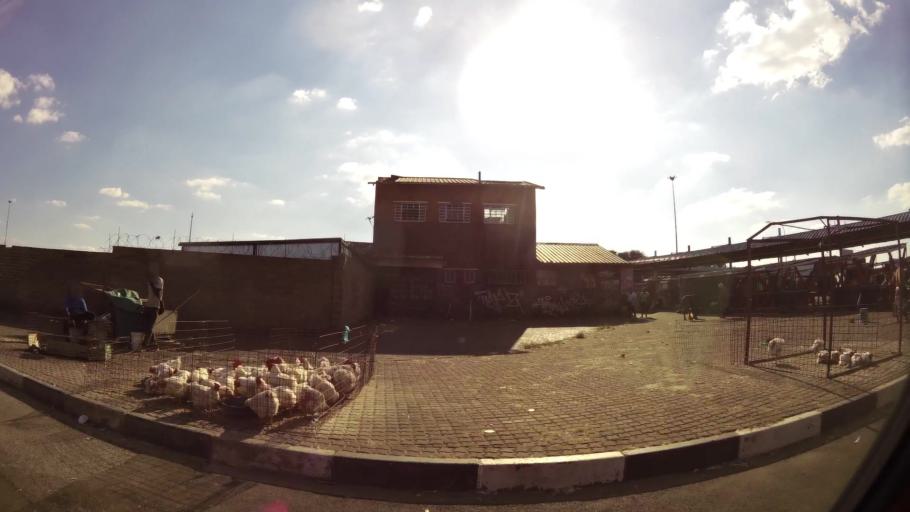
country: ZA
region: Gauteng
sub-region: City of Johannesburg Metropolitan Municipality
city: Soweto
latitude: -26.2305
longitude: 27.8765
